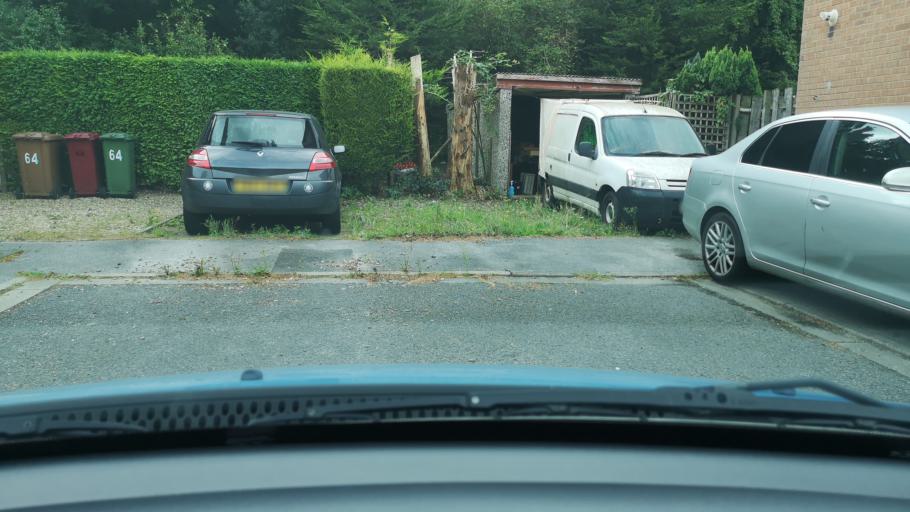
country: GB
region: England
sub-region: North Lincolnshire
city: Scunthorpe
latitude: 53.5855
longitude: -0.6867
